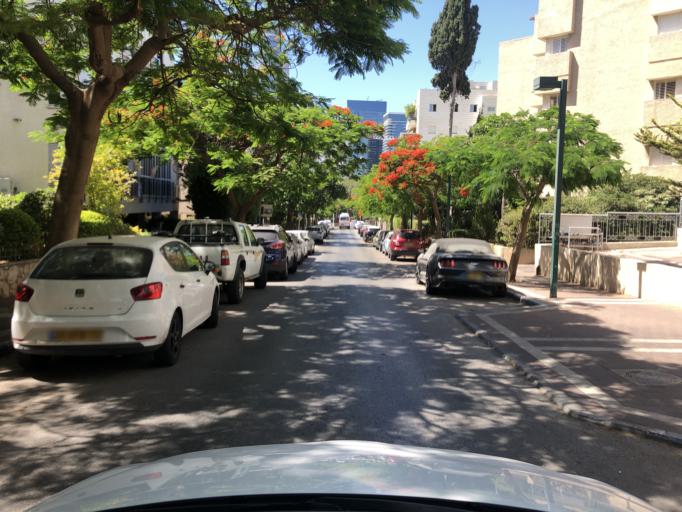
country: IL
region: Tel Aviv
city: Ramat Gan
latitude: 32.0771
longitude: 34.8063
